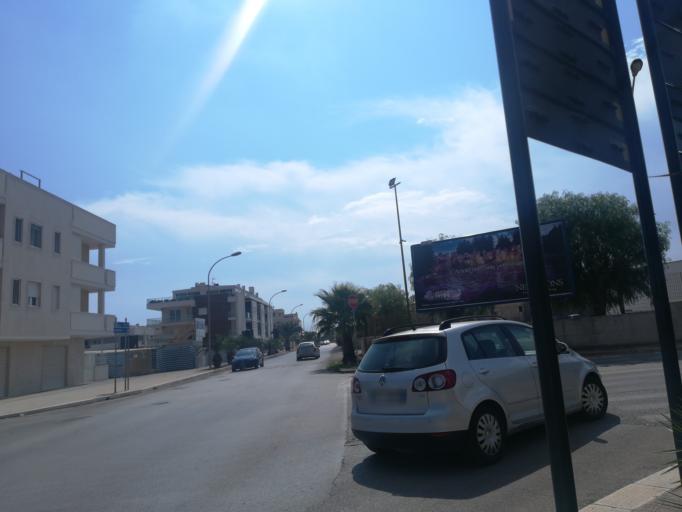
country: IT
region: Apulia
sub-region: Provincia di Bari
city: Polignano a Mare
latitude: 40.9889
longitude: 17.2309
